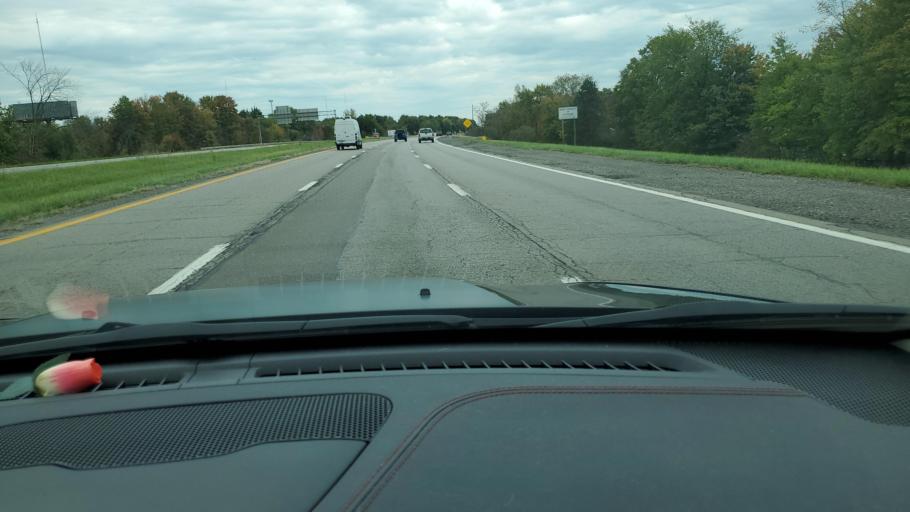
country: US
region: Ohio
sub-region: Mahoning County
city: Poland
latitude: 41.0362
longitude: -80.6312
